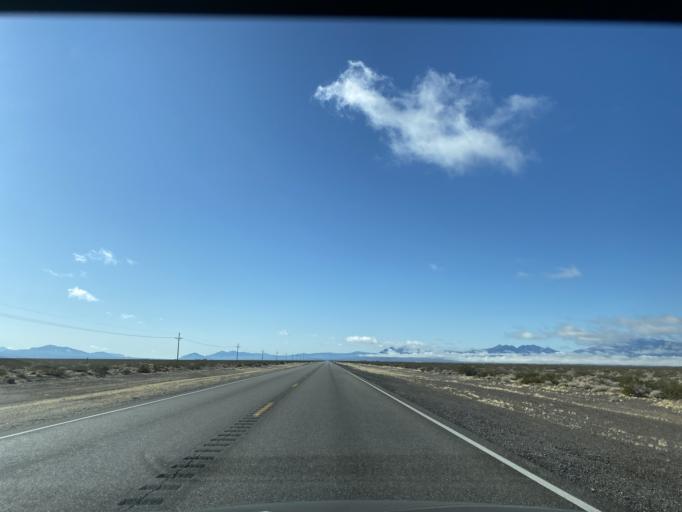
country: US
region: Nevada
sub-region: Nye County
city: Beatty
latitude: 36.6100
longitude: -116.4064
